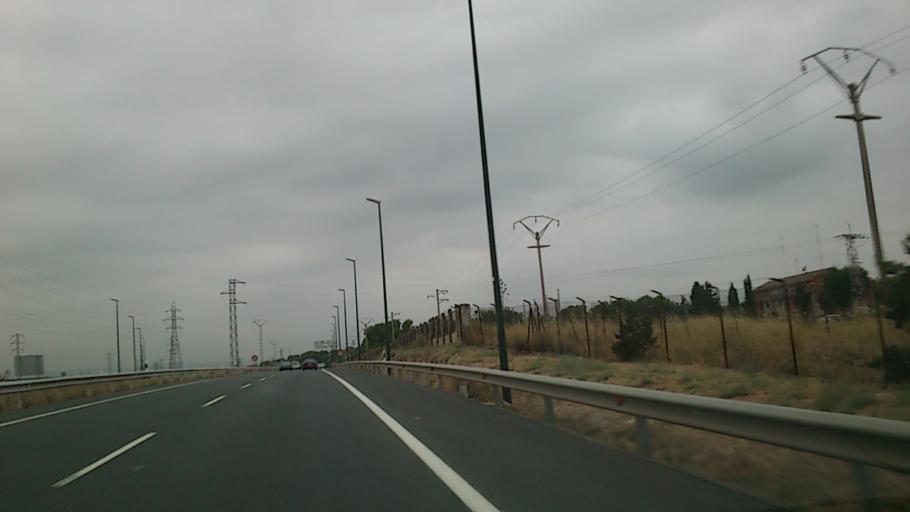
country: ES
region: Aragon
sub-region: Provincia de Zaragoza
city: Zaragoza
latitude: 41.7059
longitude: -0.8647
